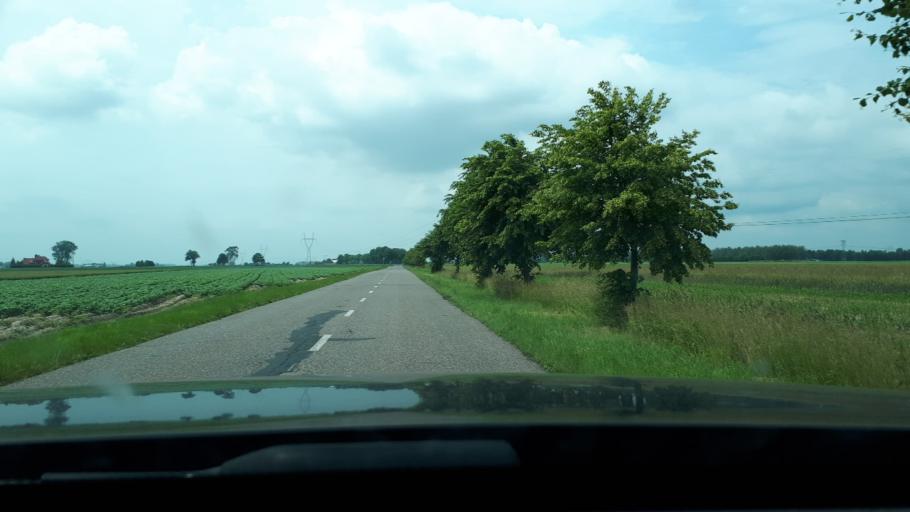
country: PL
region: Masovian Voivodeship
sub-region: Powiat warszawski zachodni
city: Jozefow
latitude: 52.2350
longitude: 20.6719
